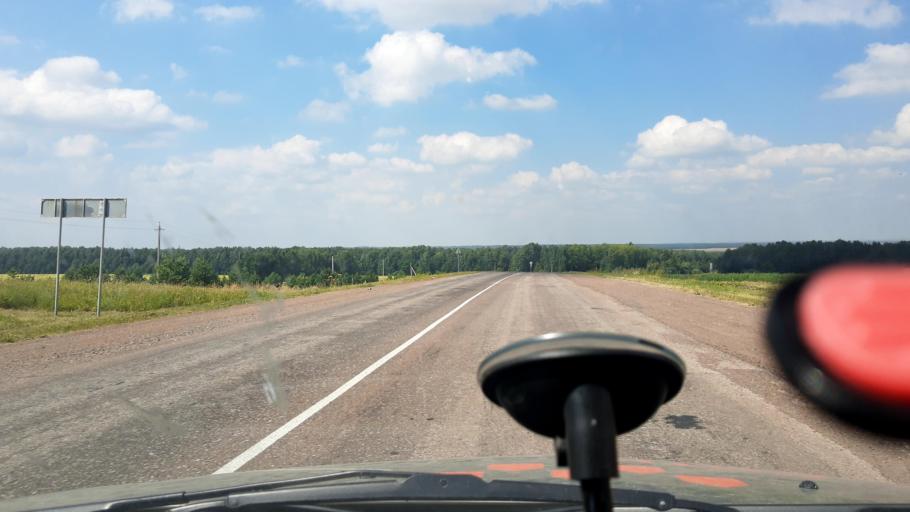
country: RU
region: Bashkortostan
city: Chekmagush
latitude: 54.9473
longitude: 54.5628
